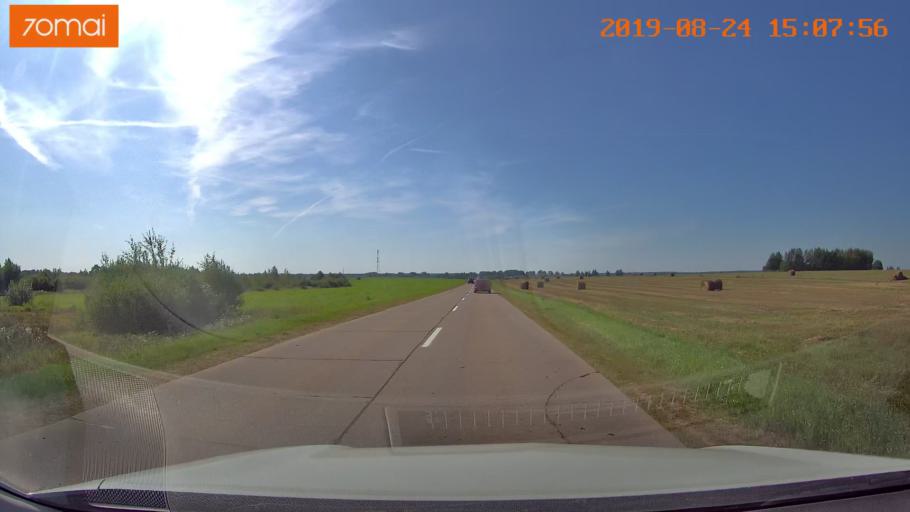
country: BY
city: Michanovichi
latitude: 53.6085
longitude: 27.6666
